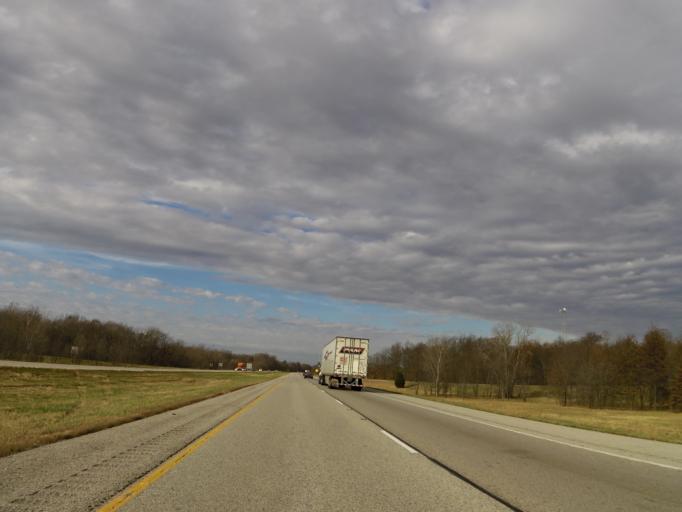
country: US
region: Illinois
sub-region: Washington County
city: Nashville
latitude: 38.3918
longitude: -89.3719
